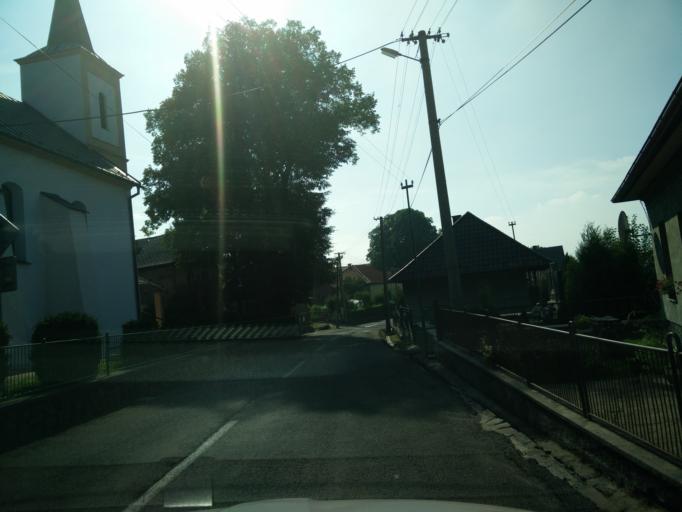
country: SK
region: Nitriansky
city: Prievidza
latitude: 48.6849
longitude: 18.6341
